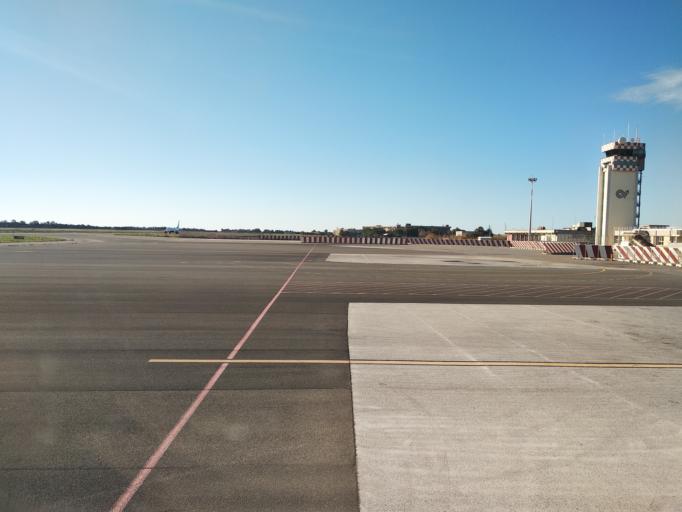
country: IT
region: Calabria
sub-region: Provincia di Catanzaro
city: Santa Eufemia Lamezia
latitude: 38.9086
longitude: 16.2446
